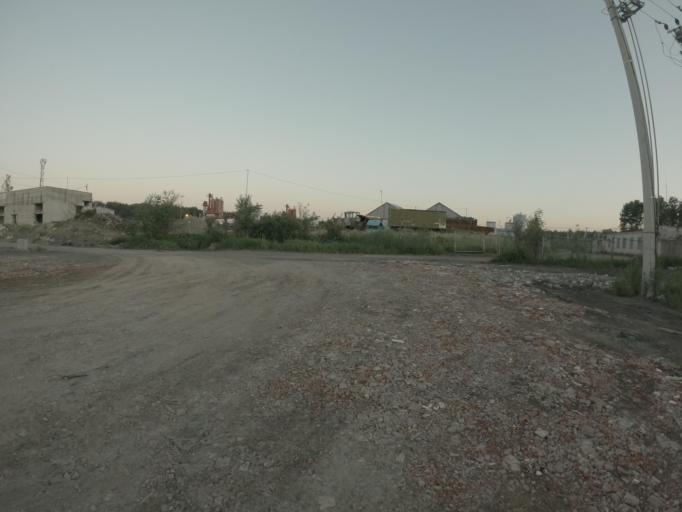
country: RU
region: Leningrad
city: Yanino Vtoroye
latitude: 59.9373
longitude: 30.5492
